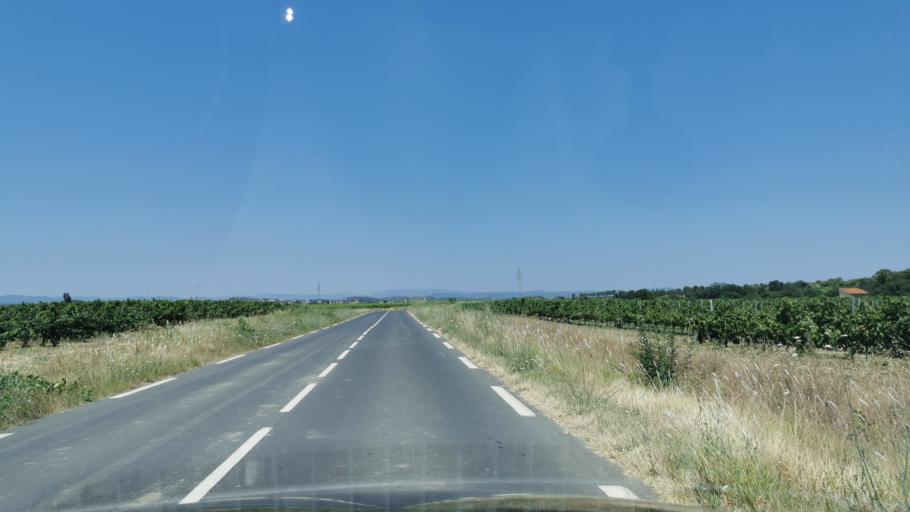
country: FR
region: Languedoc-Roussillon
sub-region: Departement de l'Herault
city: Maureilhan
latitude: 43.3678
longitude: 3.1150
